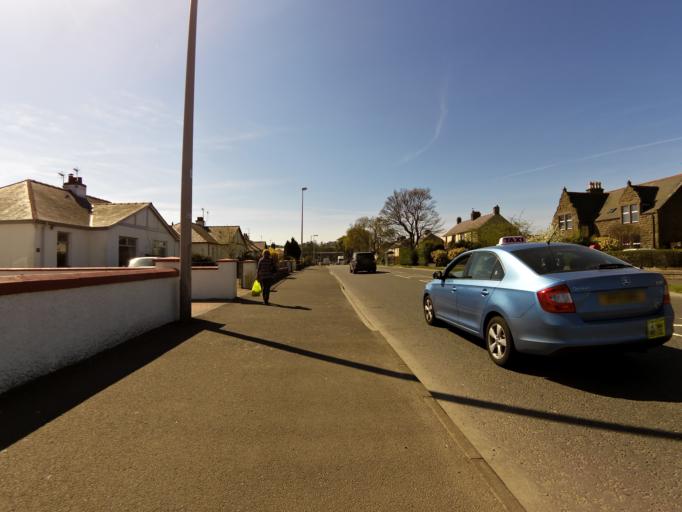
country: GB
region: Scotland
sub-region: Angus
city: Montrose
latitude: 56.7035
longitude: -2.4772
